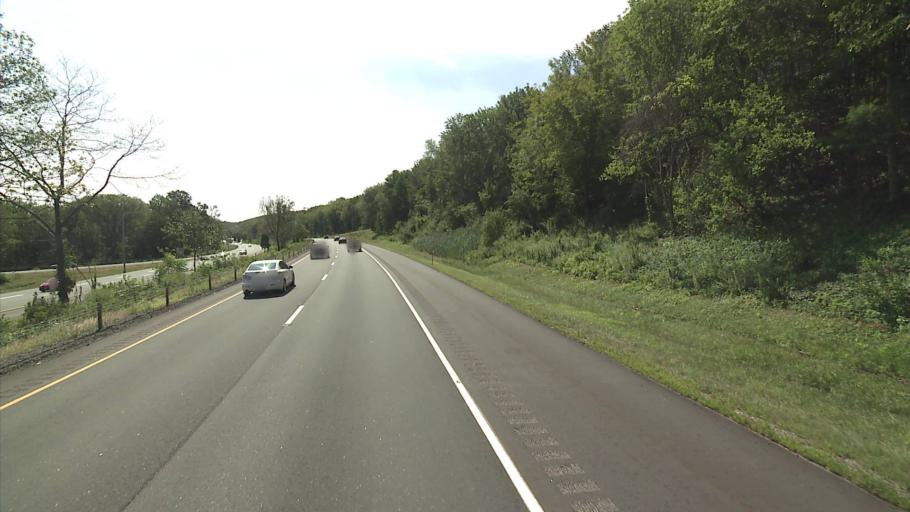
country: US
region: Connecticut
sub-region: Hartford County
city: Terramuggus
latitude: 41.6340
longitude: -72.4580
